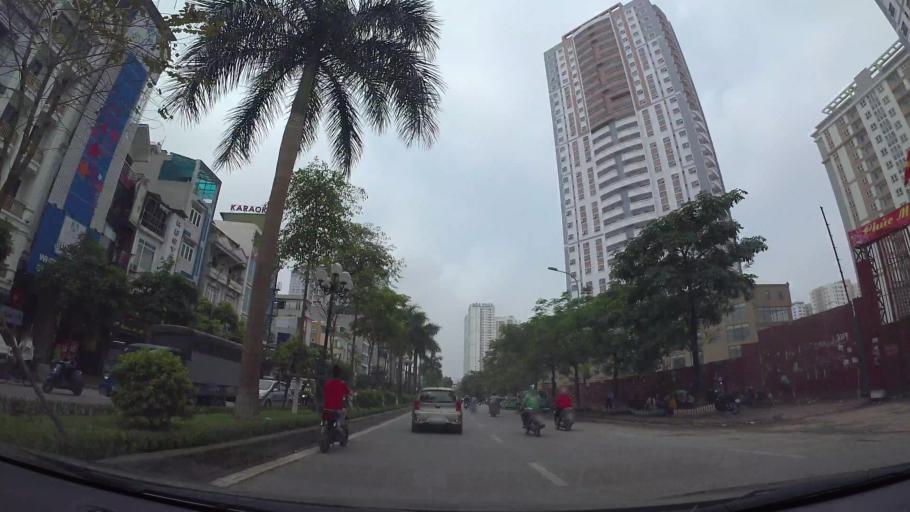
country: VN
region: Ha Noi
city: Hai BaTrung
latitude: 20.9836
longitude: 105.8525
